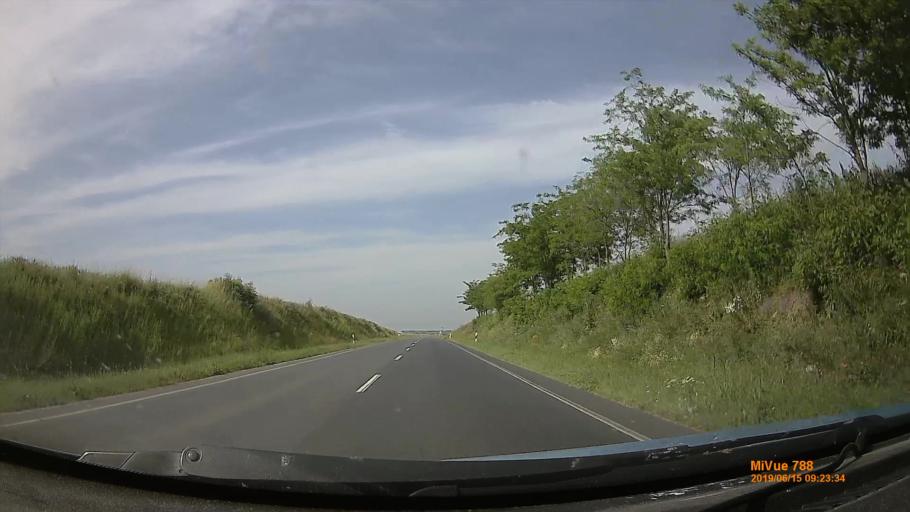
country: HU
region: Tolna
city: Iregszemcse
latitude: 46.5632
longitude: 18.1688
